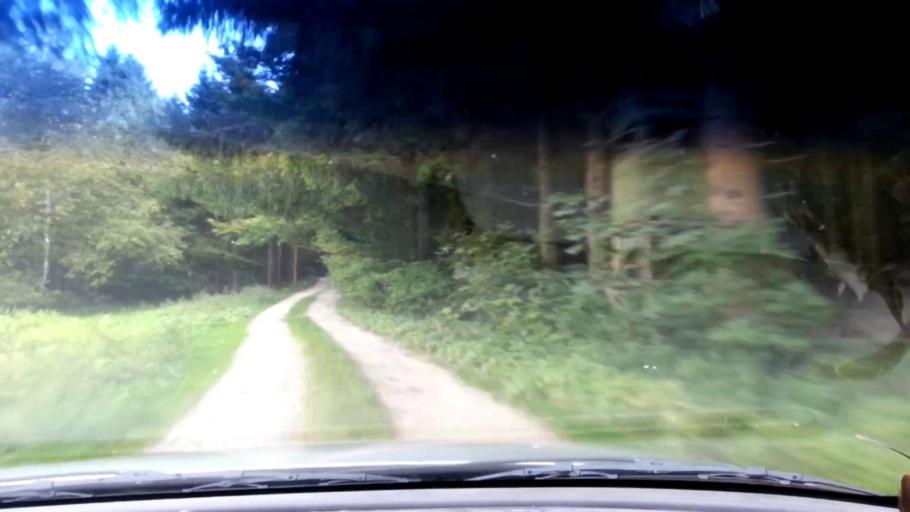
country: DE
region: Bavaria
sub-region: Upper Franconia
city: Wattendorf
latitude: 49.9965
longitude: 11.1064
